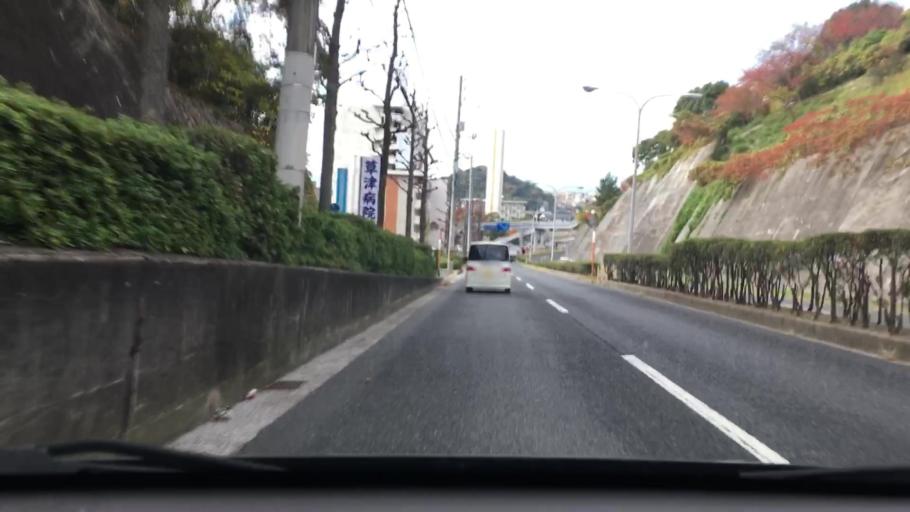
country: JP
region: Hiroshima
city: Hatsukaichi
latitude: 34.3787
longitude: 132.3936
